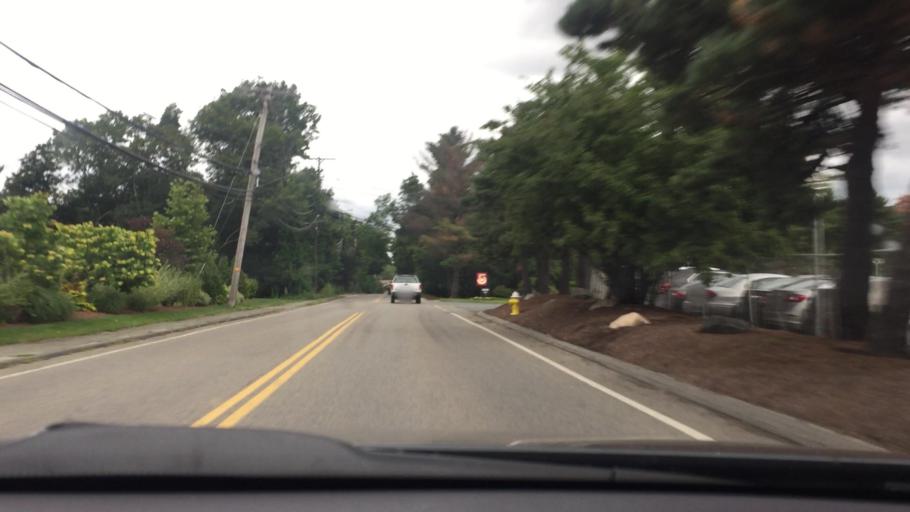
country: US
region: Massachusetts
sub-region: Norfolk County
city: Needham
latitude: 42.3020
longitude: -71.2297
